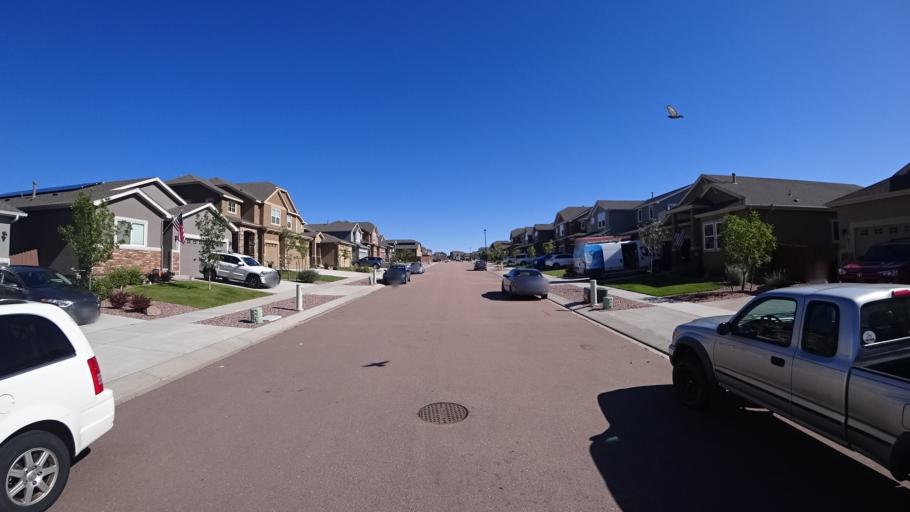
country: US
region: Colorado
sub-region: El Paso County
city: Black Forest
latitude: 38.9471
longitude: -104.6738
